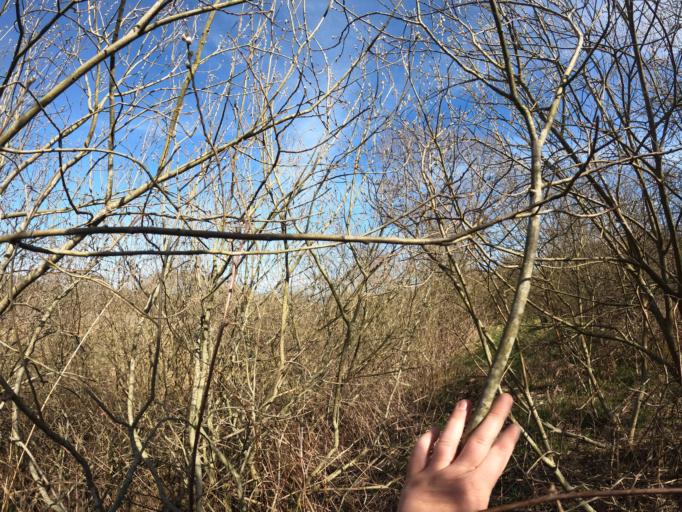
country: PL
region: West Pomeranian Voivodeship
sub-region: Powiat gryficki
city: Brojce
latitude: 53.9234
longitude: 15.3043
